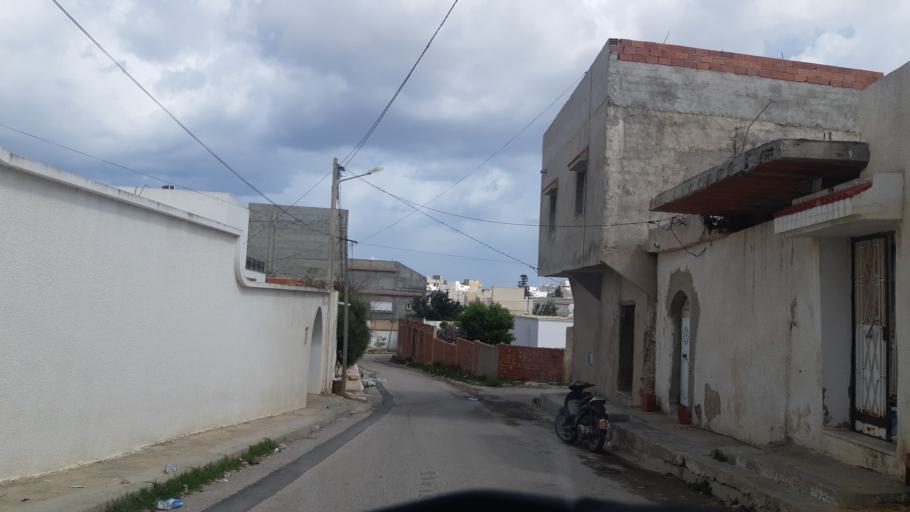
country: TN
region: Susah
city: Akouda
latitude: 35.8634
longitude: 10.5435
